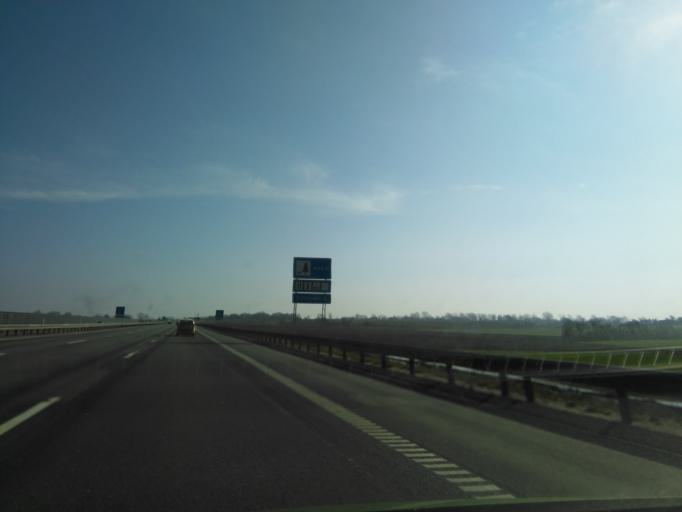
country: DK
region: South Denmark
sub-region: Middelfart Kommune
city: Norre Aby
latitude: 55.4831
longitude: 9.8625
